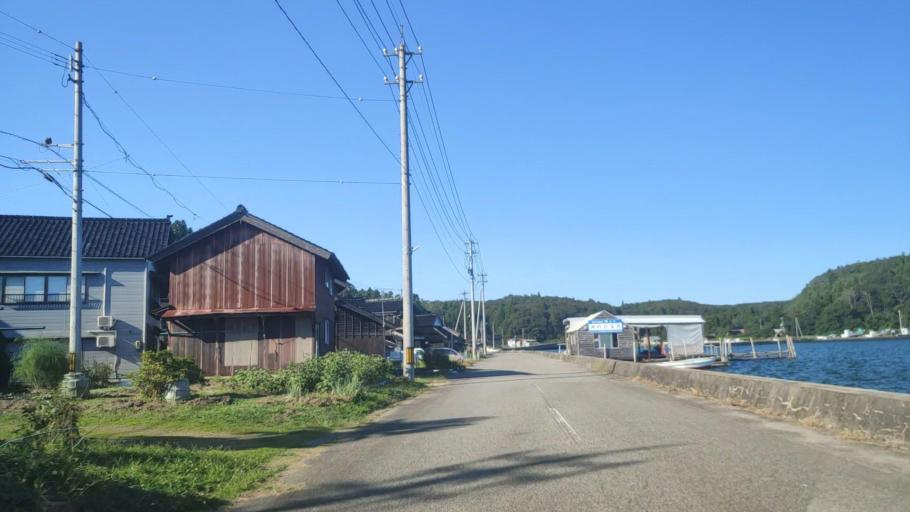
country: JP
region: Ishikawa
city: Nanao
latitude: 37.1119
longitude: 136.8817
